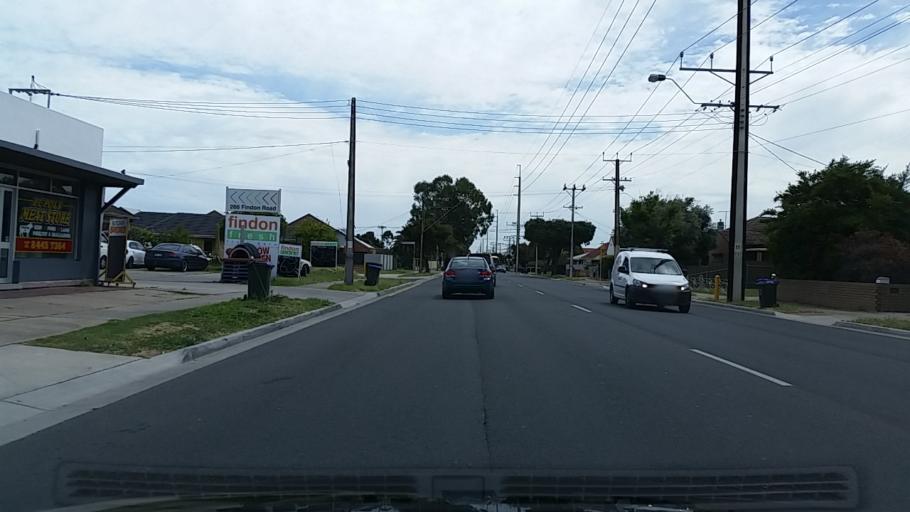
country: AU
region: South Australia
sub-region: Charles Sturt
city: Findon
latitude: -34.9015
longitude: 138.5323
